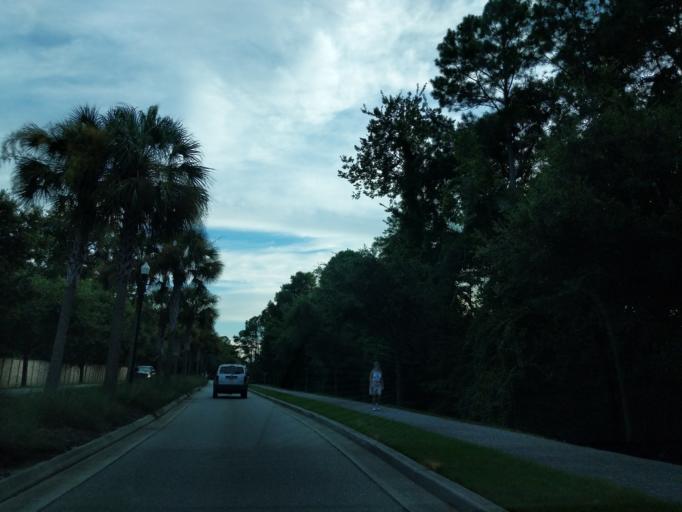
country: US
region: South Carolina
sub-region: Charleston County
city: Isle of Palms
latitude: 32.8330
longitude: -79.8209
